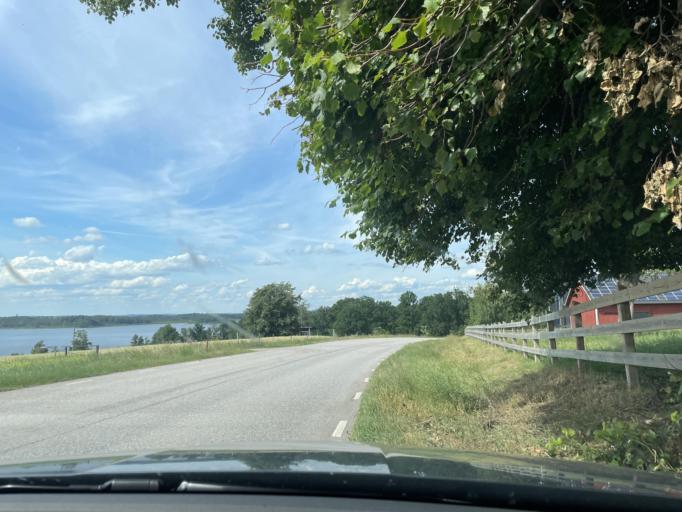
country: SE
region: Kalmar
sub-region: Vimmerby Kommun
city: Sodra Vi
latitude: 57.7155
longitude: 15.8367
